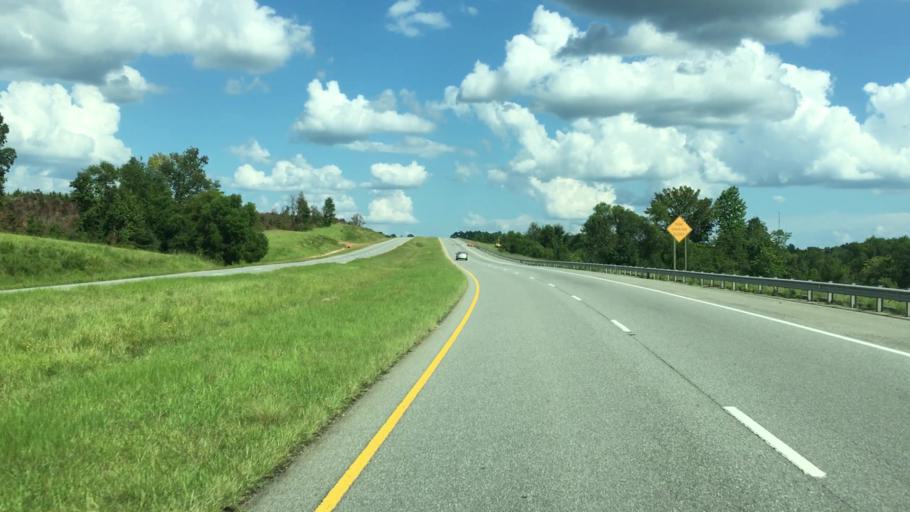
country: US
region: Georgia
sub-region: Wilkinson County
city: Irwinton
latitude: 32.6962
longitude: -83.1152
